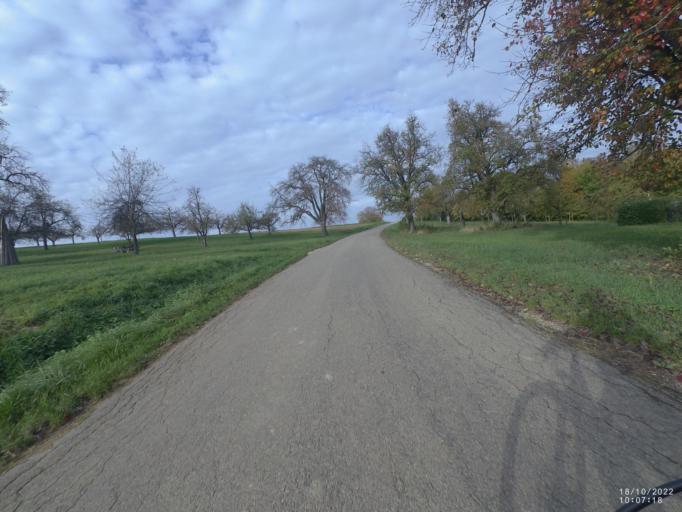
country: DE
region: Baden-Wuerttemberg
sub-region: Regierungsbezirk Stuttgart
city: Sussen
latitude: 48.6779
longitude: 9.7416
